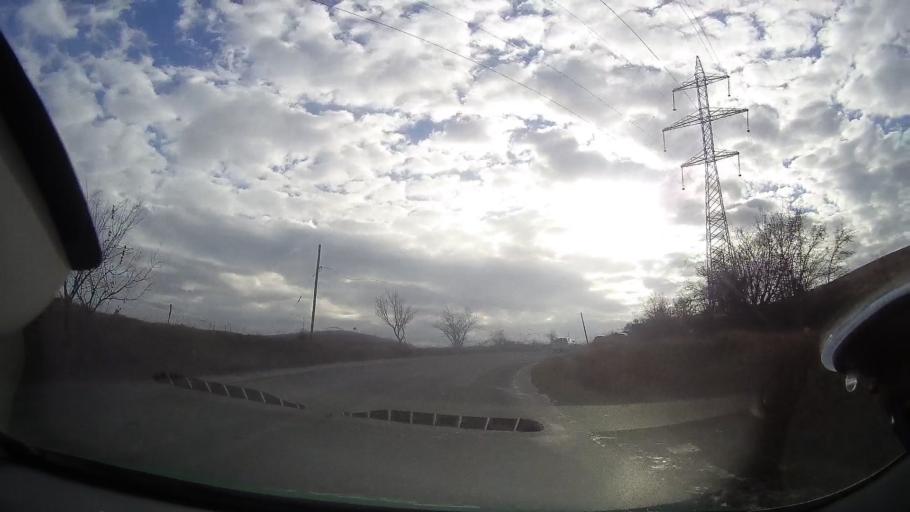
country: RO
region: Cluj
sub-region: Comuna Savadisla
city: Savadisla
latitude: 46.6557
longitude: 23.4519
